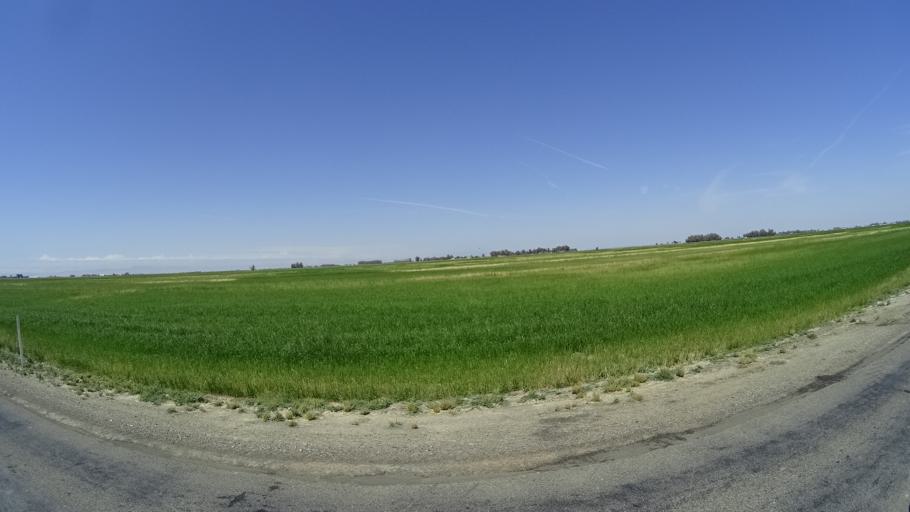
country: US
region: California
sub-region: Kings County
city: Stratford
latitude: 36.1933
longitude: -119.7624
